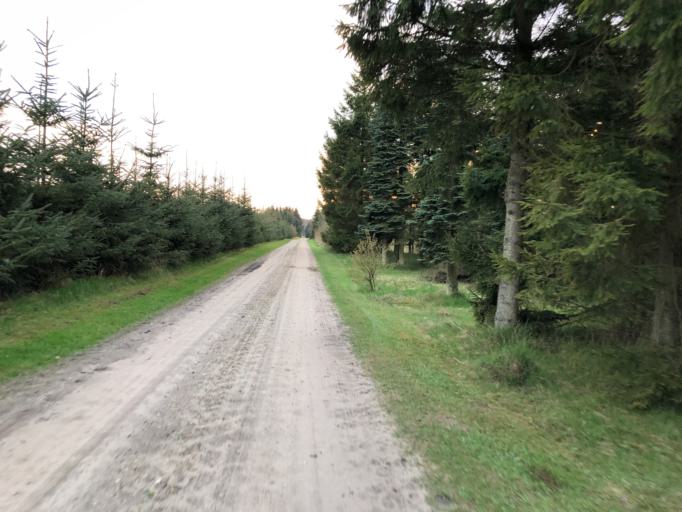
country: DK
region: Central Jutland
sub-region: Holstebro Kommune
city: Ulfborg
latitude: 56.2248
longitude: 8.4192
